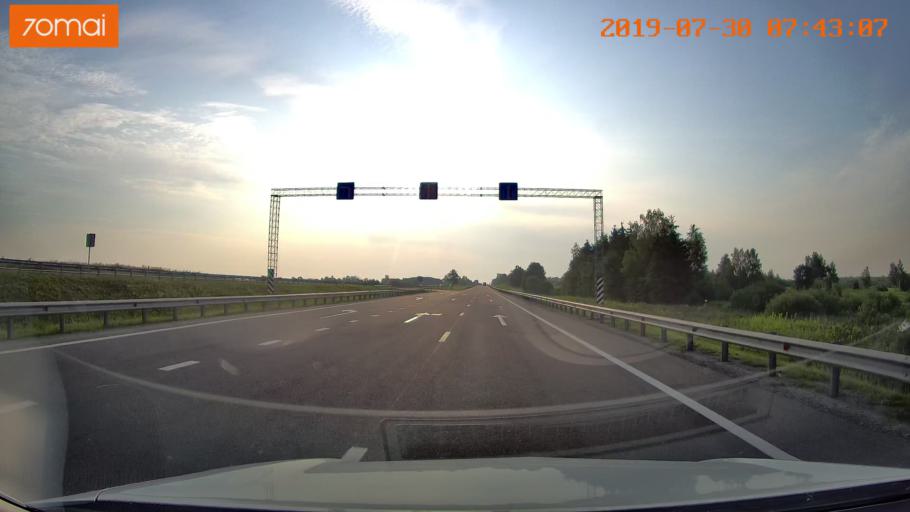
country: RU
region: Kaliningrad
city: Gvardeysk
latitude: 54.6487
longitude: 21.2976
